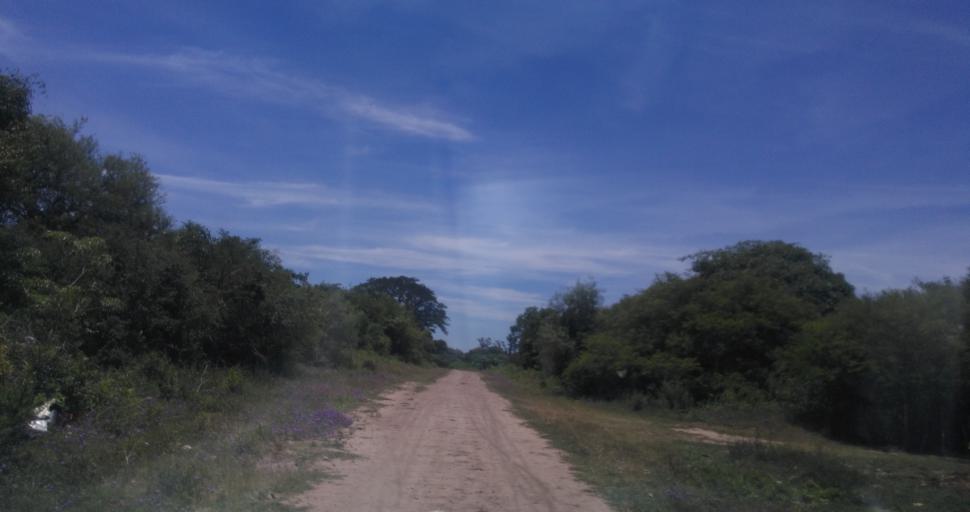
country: AR
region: Chaco
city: Fontana
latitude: -27.4272
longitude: -59.0476
